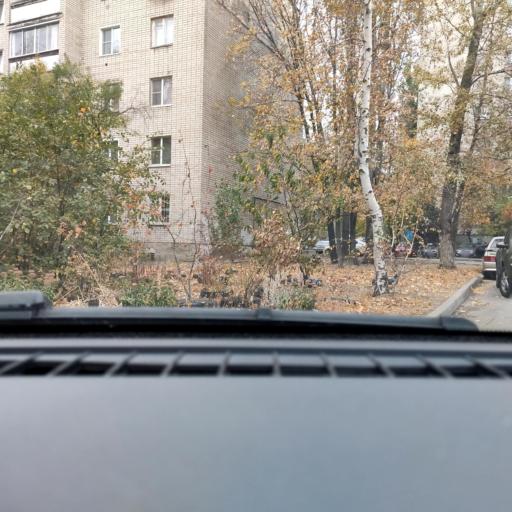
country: RU
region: Voronezj
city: Podgornoye
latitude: 51.6998
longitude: 39.1474
